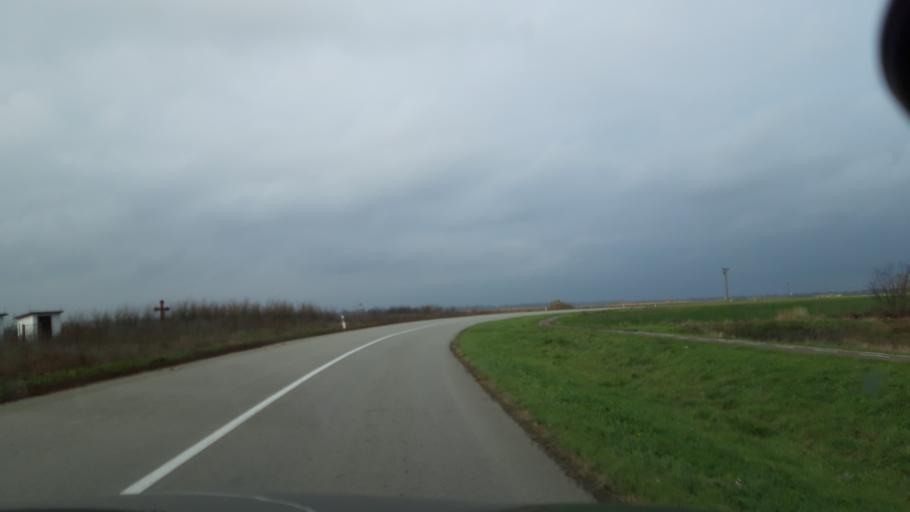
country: RS
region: Autonomna Pokrajina Vojvodina
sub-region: Severnobanatski Okrug
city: Kanjiza
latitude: 46.1322
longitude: 20.0927
